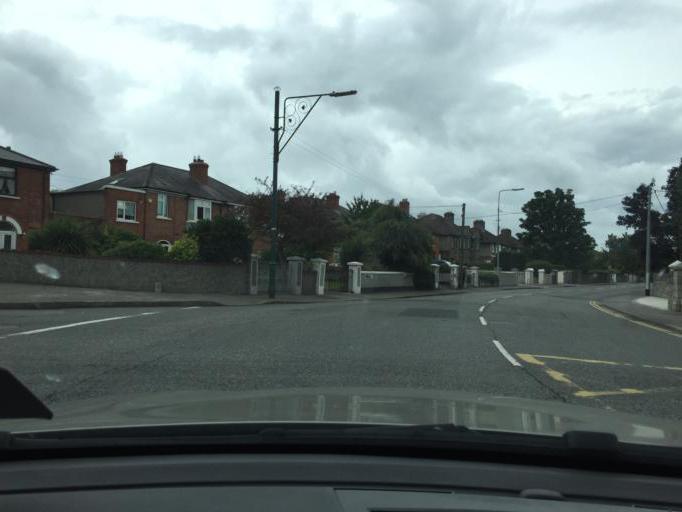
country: IE
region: Leinster
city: Crumlin
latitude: 53.3192
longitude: -6.3151
